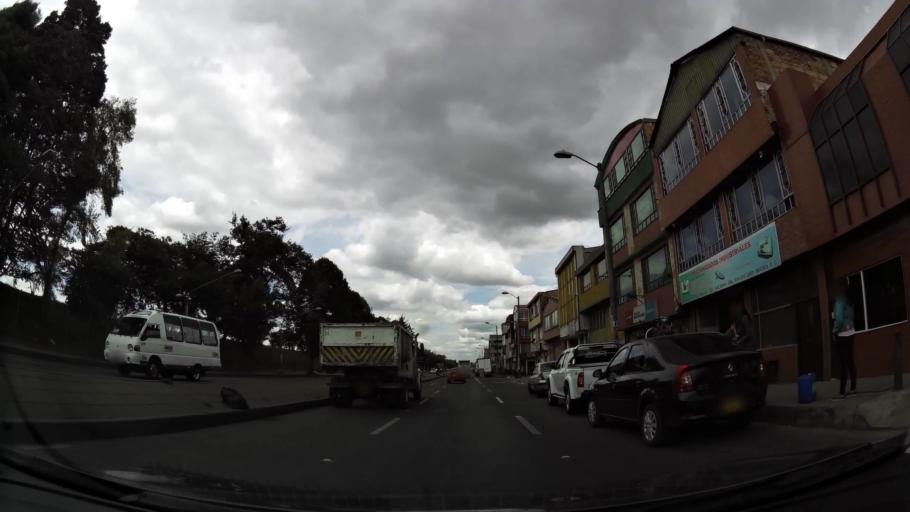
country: CO
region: Cundinamarca
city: Funza
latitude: 4.6991
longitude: -74.1295
